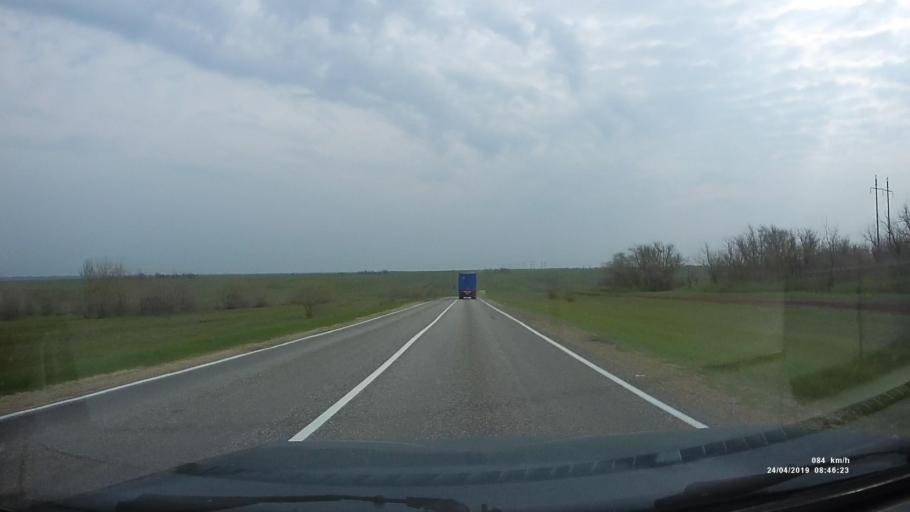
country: RU
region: Kalmykiya
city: Arshan'
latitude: 46.2384
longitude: 44.0779
